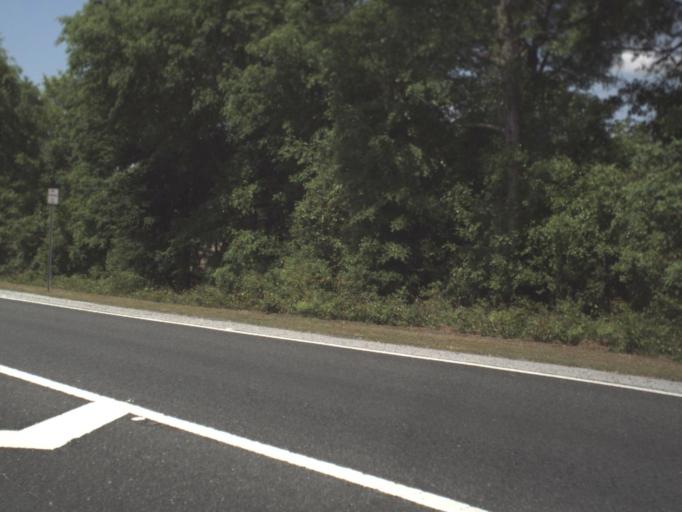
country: US
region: Florida
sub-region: Santa Rosa County
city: East Milton
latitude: 30.6092
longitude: -86.9807
